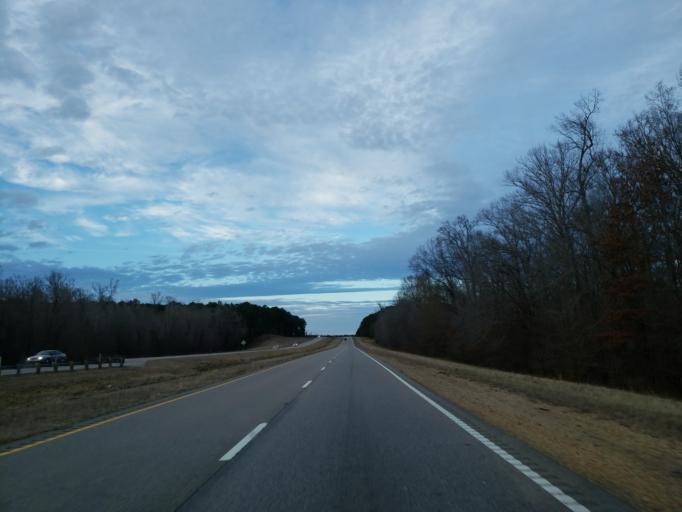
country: US
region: Mississippi
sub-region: Kemper County
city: De Kalb
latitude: 32.7044
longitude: -88.4831
